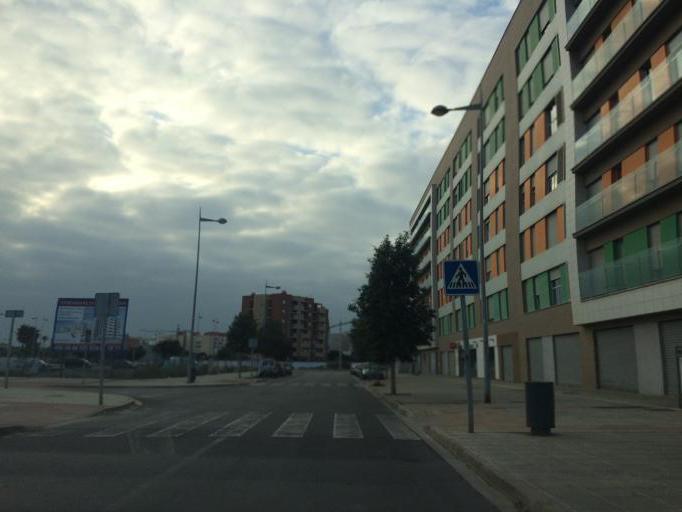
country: ES
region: Andalusia
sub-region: Provincia de Almeria
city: Almeria
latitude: 36.8285
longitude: -2.4423
